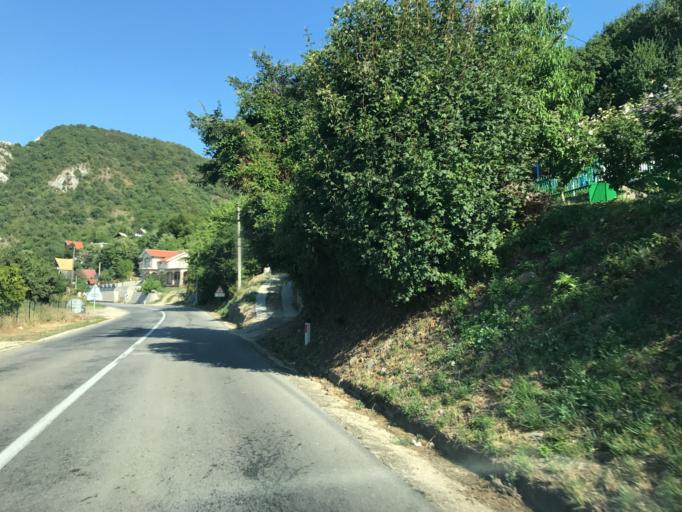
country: RO
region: Caras-Severin
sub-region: Comuna Pescari
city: Coronini
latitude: 44.6601
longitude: 21.6862
